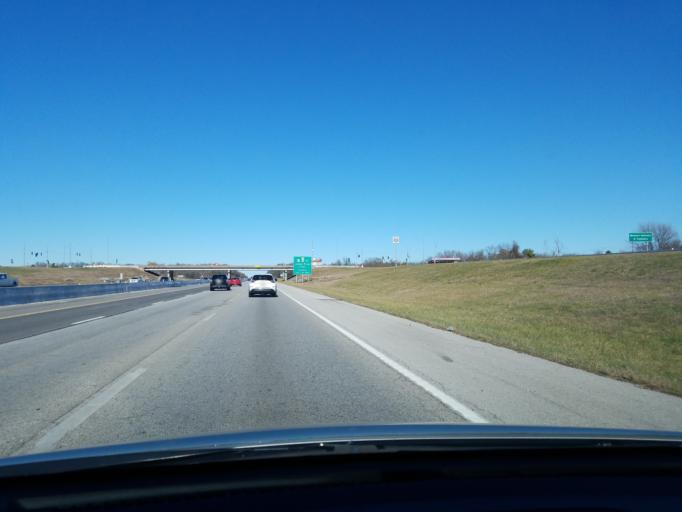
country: US
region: Missouri
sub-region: Christian County
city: Ozark
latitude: 37.0983
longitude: -93.2319
